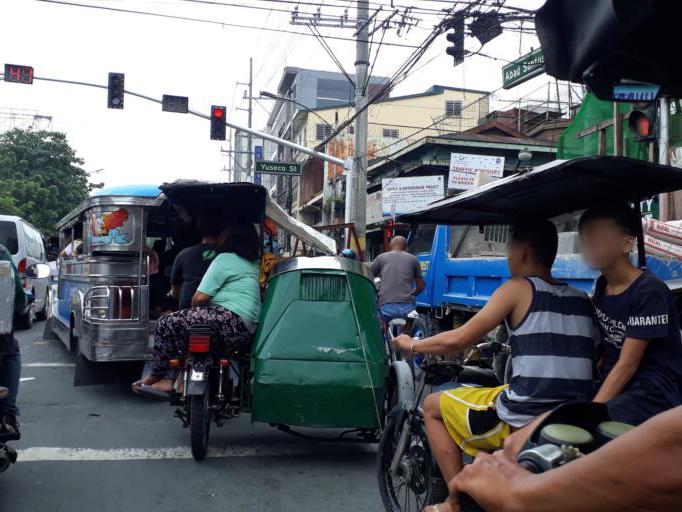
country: PH
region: Metro Manila
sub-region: City of Manila
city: Manila
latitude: 14.6199
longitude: 120.9776
